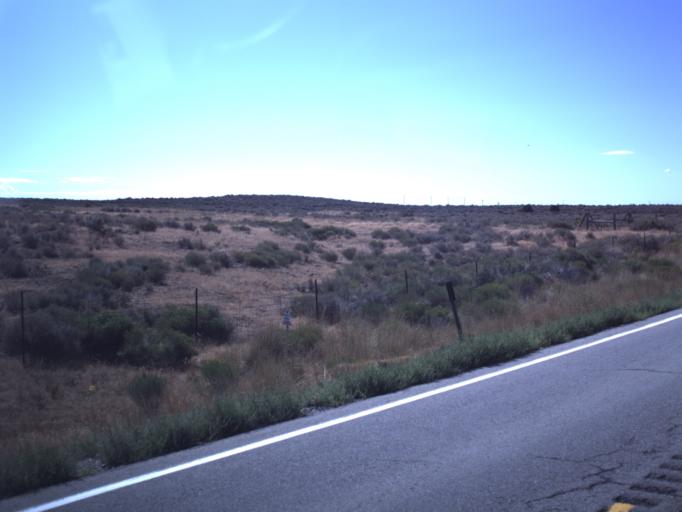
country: US
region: Utah
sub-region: Tooele County
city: Tooele
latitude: 40.4154
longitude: -112.3832
